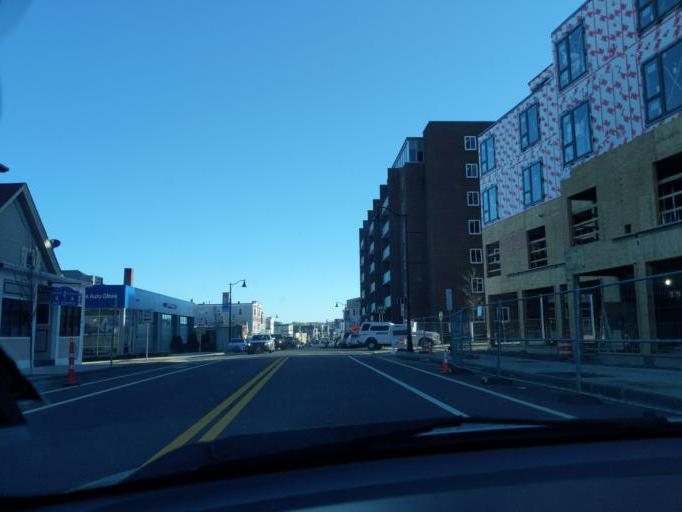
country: US
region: Massachusetts
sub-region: Essex County
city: Beverly
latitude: 42.5484
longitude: -70.8839
